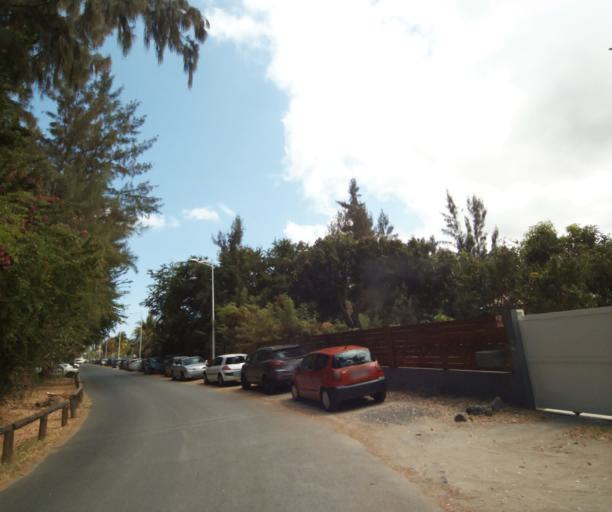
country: RE
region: Reunion
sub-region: Reunion
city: Trois-Bassins
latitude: -21.0886
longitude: 55.2312
